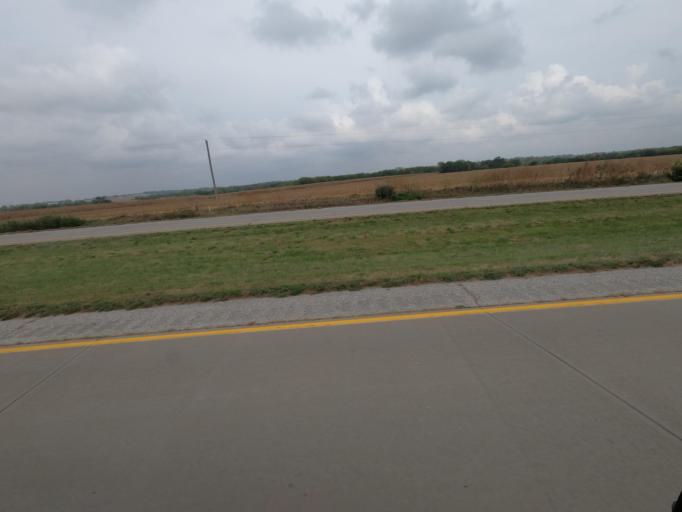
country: US
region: Iowa
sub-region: Wapello County
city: Eddyville
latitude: 41.1244
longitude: -92.5622
